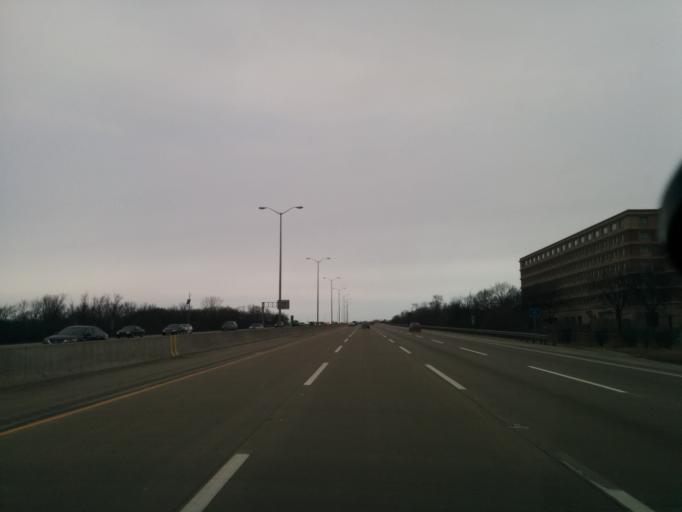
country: US
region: Illinois
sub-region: Cook County
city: Des Plaines
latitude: 42.0783
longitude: -87.8663
